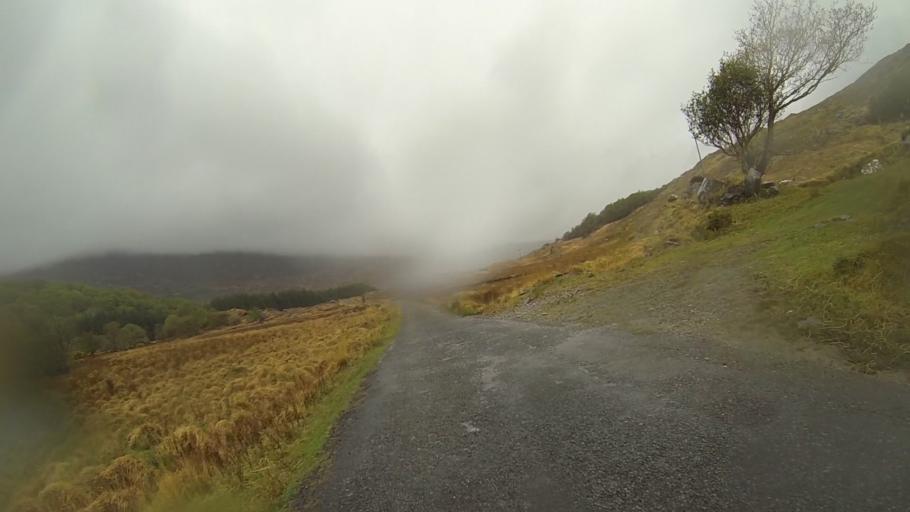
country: IE
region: Munster
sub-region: Ciarrai
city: Kenmare
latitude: 51.9565
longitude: -9.6361
